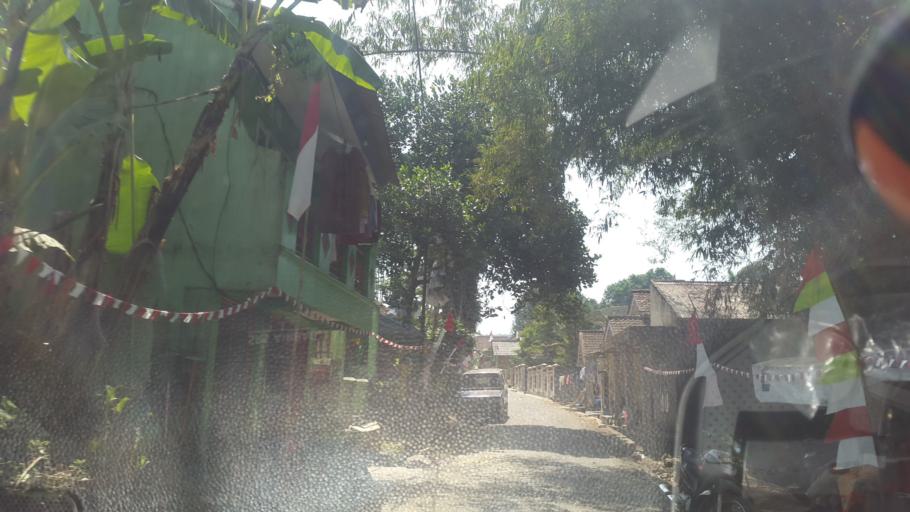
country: ID
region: West Java
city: Cicurug
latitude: -6.8729
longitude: 106.7808
